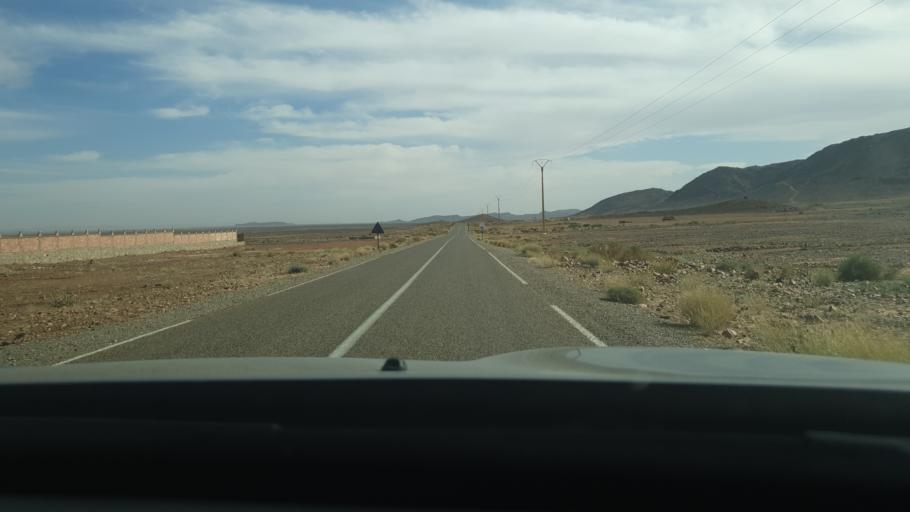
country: MA
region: Meknes-Tafilalet
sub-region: Errachidia
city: Fezna
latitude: 31.5282
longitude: -4.6354
